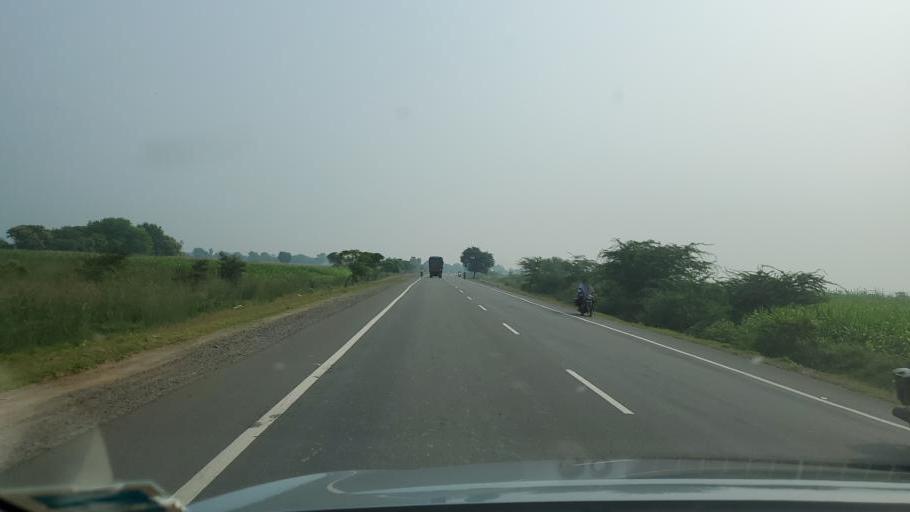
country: IN
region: Tamil Nadu
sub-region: Perambalur
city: Perambalur
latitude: 11.2400
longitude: 79.0018
